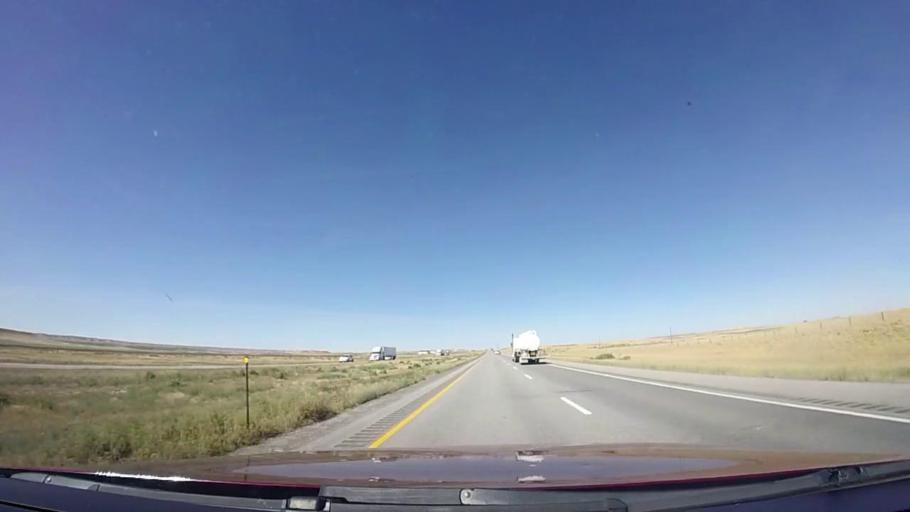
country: US
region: Wyoming
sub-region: Carbon County
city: Rawlins
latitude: 41.6551
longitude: -108.1092
